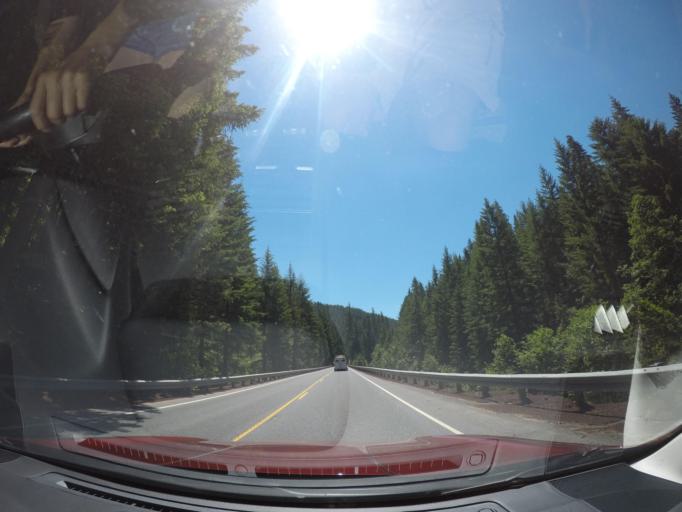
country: US
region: Oregon
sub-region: Deschutes County
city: Sisters
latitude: 44.5569
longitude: -121.9964
